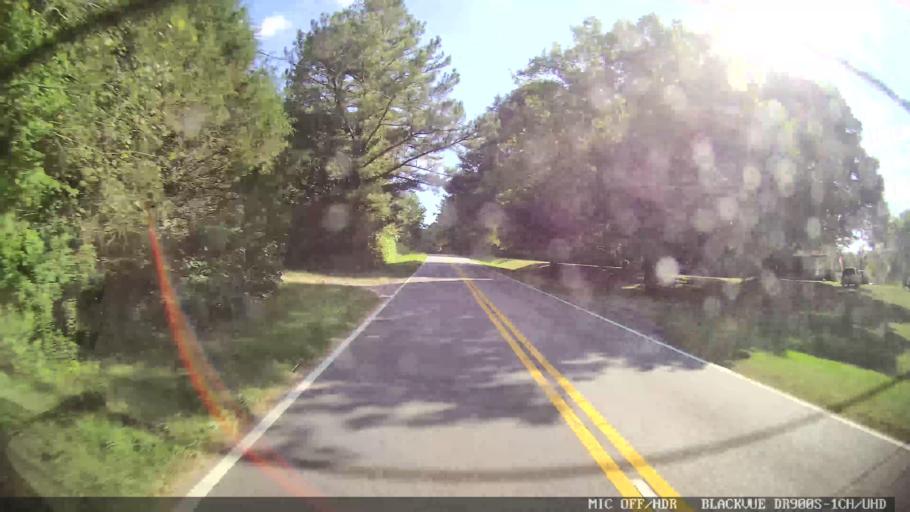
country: US
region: Georgia
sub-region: Bartow County
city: Euharlee
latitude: 34.1722
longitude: -84.9823
